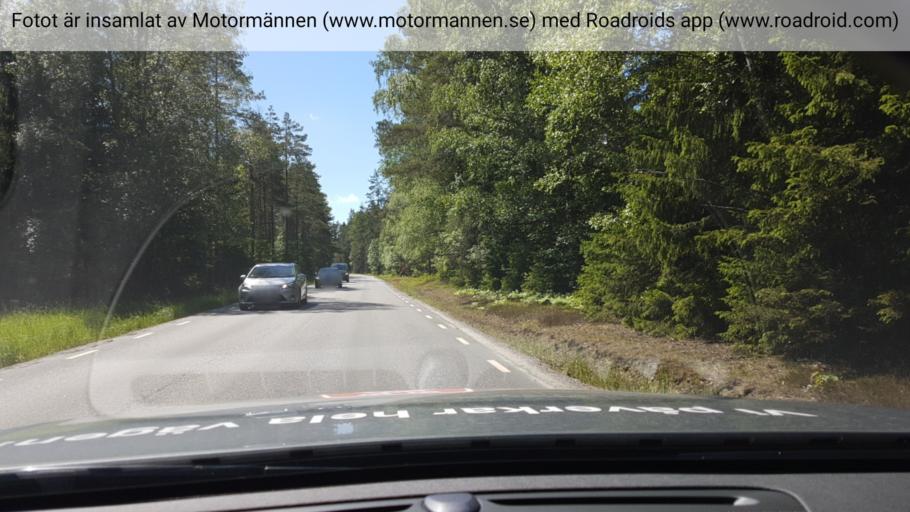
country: SE
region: Stockholm
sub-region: Haninge Kommun
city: Haninge
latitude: 59.1598
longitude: 18.1813
